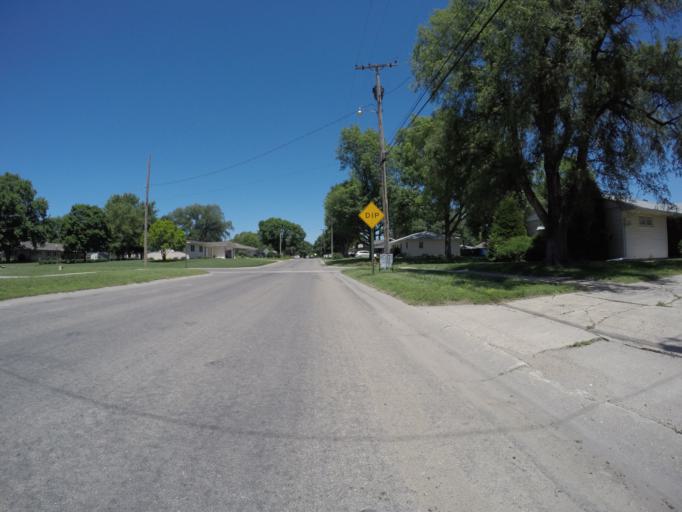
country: US
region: Kansas
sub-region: Republic County
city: Belleville
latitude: 39.8156
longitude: -97.6282
